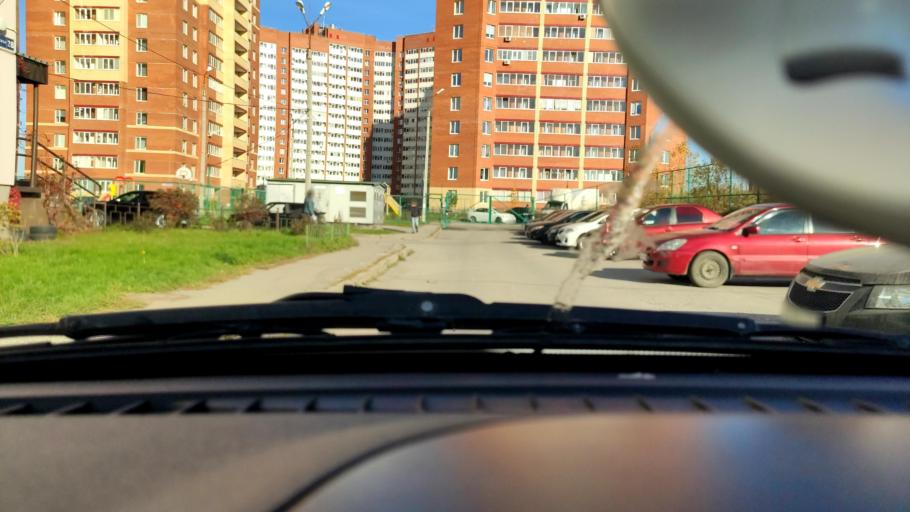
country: RU
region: Perm
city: Perm
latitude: 57.9840
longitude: 56.2834
